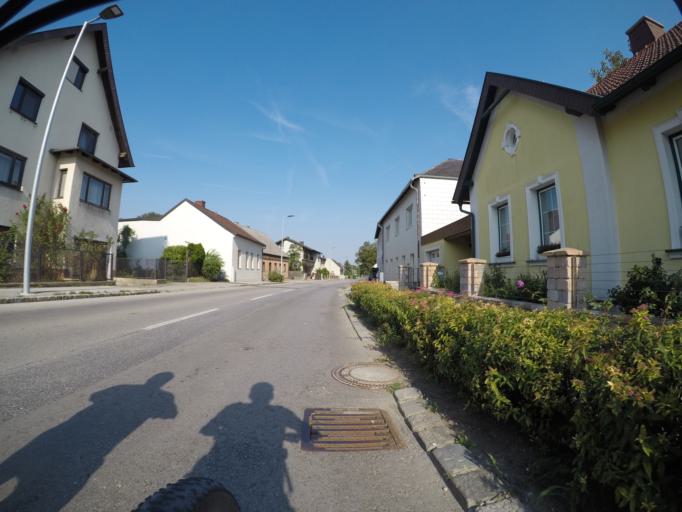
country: AT
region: Lower Austria
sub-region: Politischer Bezirk Baden
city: Hirtenberg
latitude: 47.9573
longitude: 16.1710
